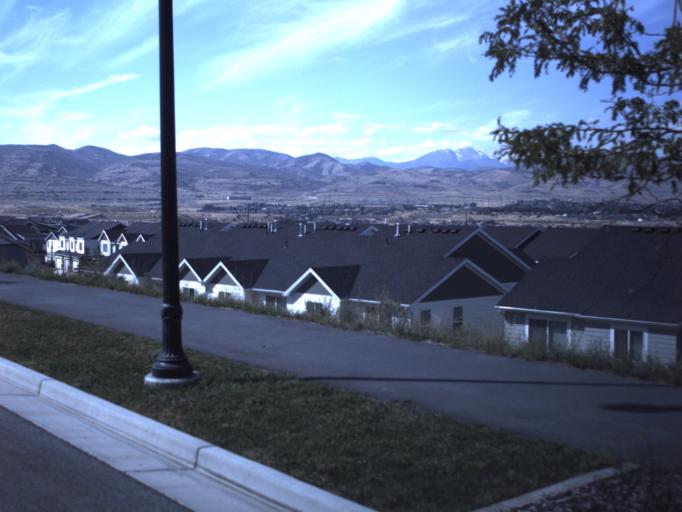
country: US
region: Utah
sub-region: Salt Lake County
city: Bluffdale
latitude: 40.4769
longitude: -111.9101
